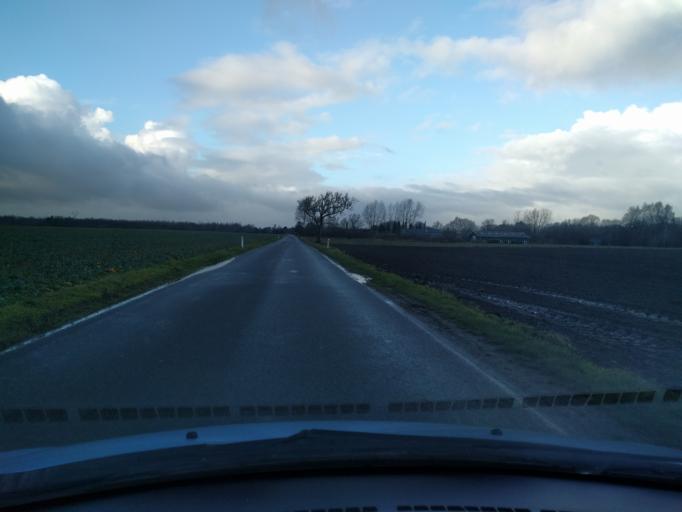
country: DK
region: South Denmark
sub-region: Kerteminde Kommune
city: Langeskov
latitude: 55.3902
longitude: 10.5717
